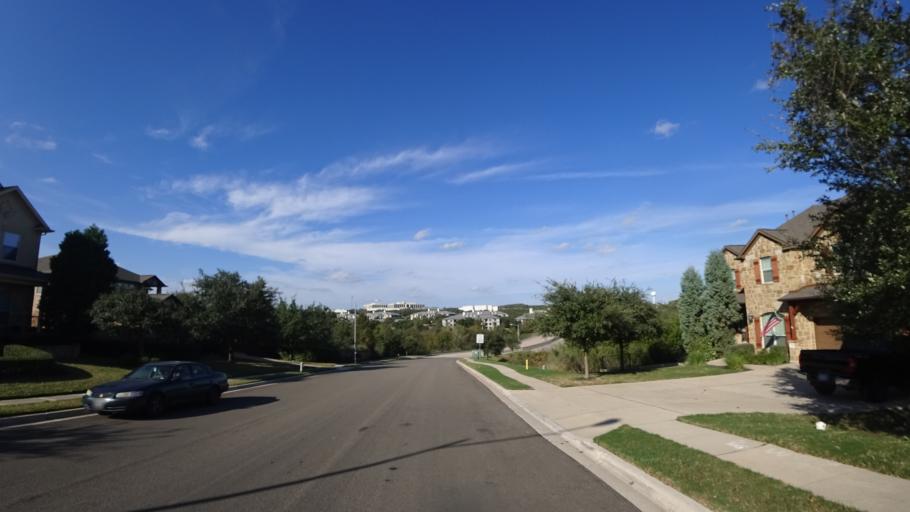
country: US
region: Texas
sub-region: Travis County
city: Barton Creek
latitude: 30.2482
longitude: -97.8701
